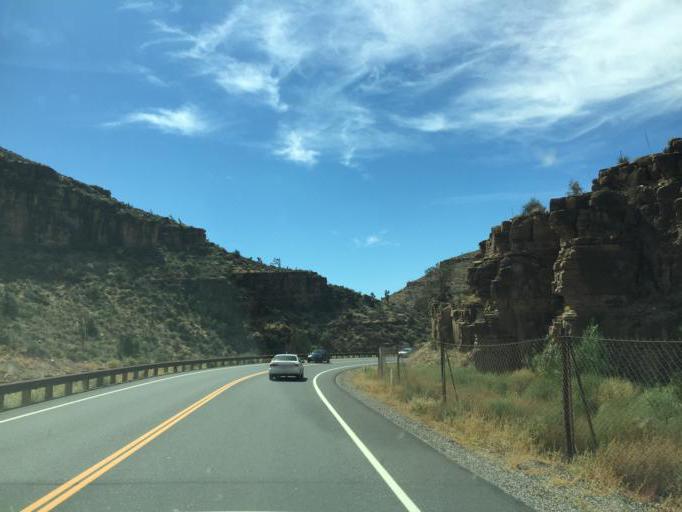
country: US
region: Arizona
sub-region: Mohave County
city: Meadview
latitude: 35.9053
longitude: -113.9338
